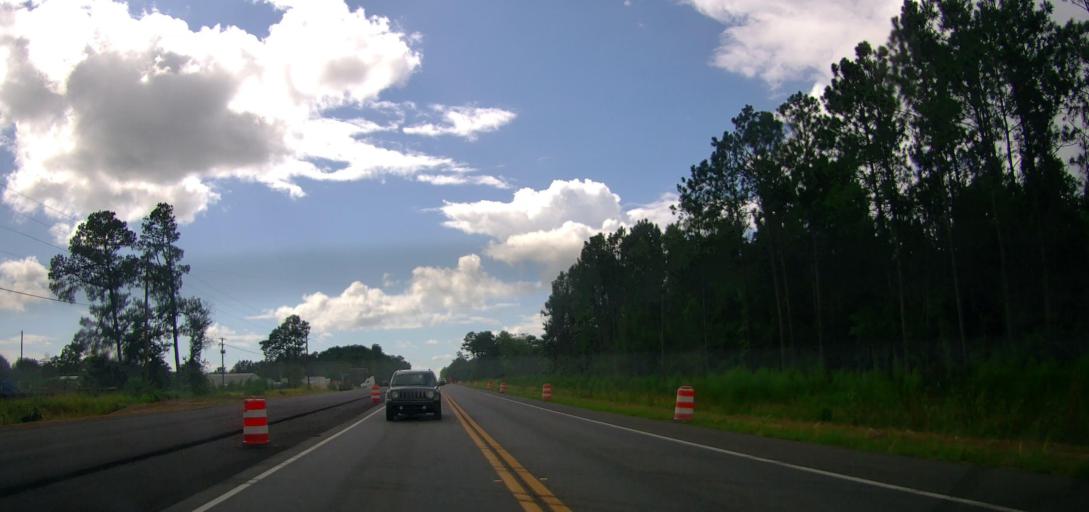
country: US
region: Georgia
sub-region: Coffee County
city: Douglas
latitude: 31.5229
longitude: -82.8964
